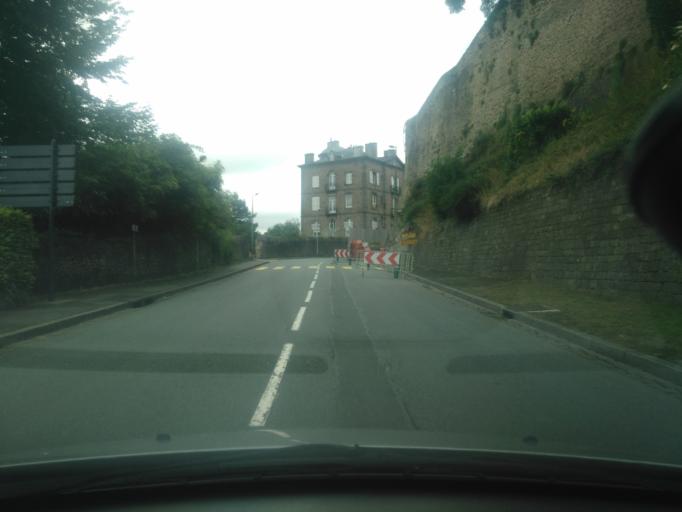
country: FR
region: Brittany
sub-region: Departement des Cotes-d'Armor
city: Dinan
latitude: 48.4534
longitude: -2.0392
